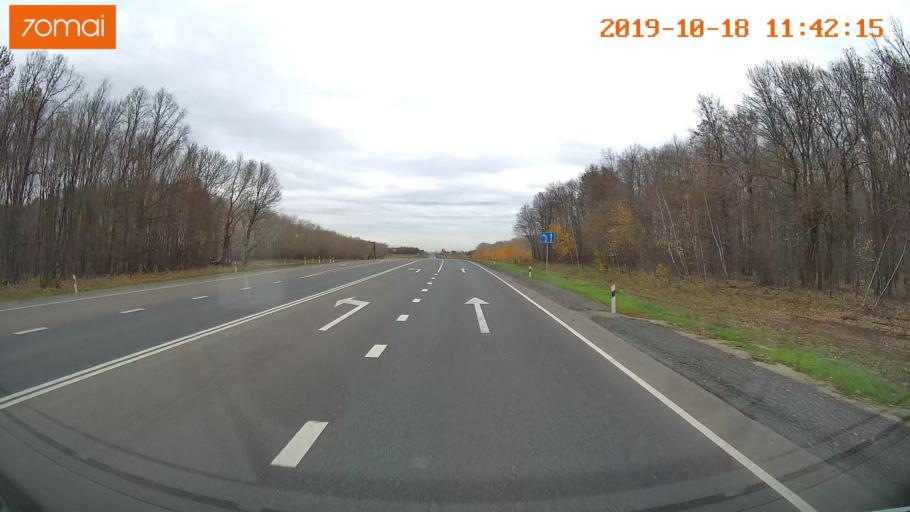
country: RU
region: Rjazan
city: Oktyabr'skiy
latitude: 54.1863
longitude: 38.9238
